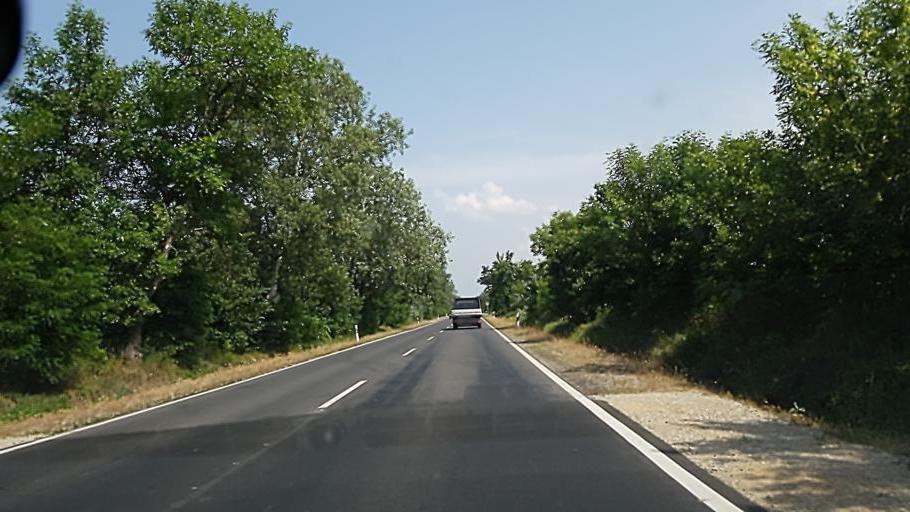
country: HU
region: Heves
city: Poroszlo
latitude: 47.6513
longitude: 20.6166
